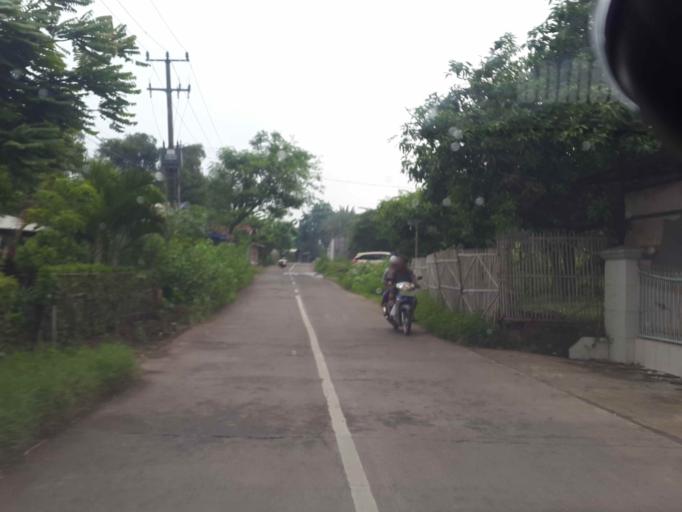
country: ID
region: West Java
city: Cikarang
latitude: -6.3083
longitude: 107.1828
